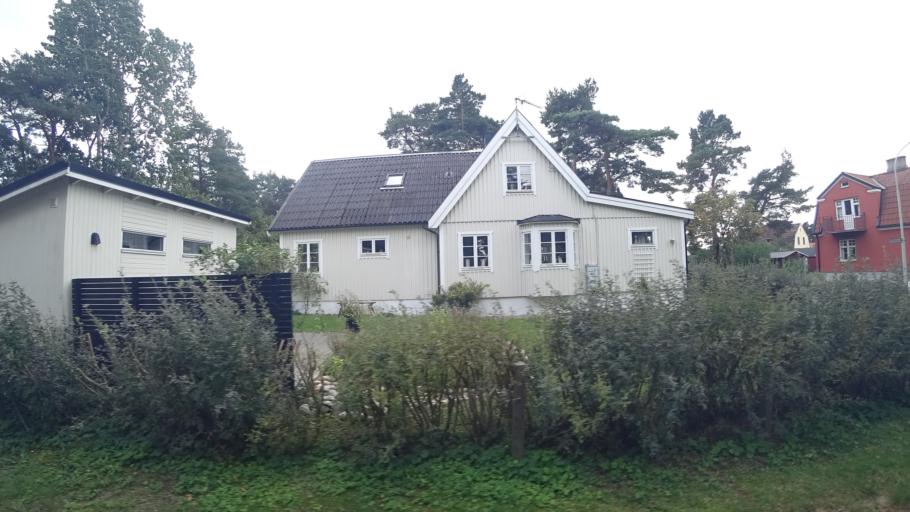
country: SE
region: Skane
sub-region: Kristianstads Kommun
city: Ahus
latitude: 55.9328
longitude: 14.3106
